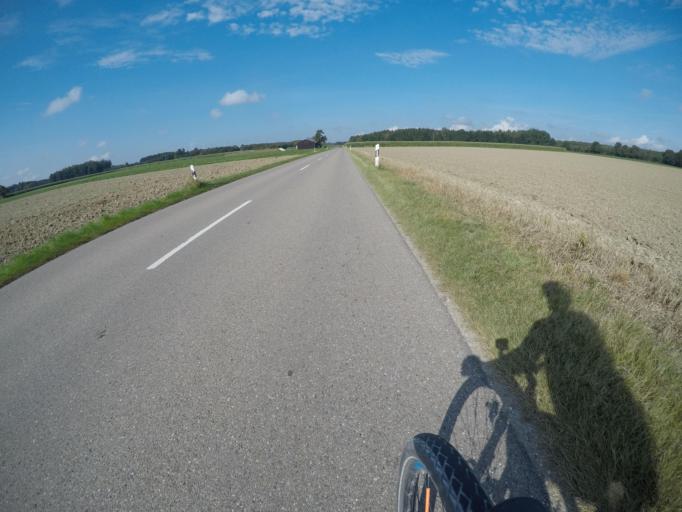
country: DE
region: Bavaria
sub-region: Swabia
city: Allmannshofen
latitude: 48.6141
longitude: 10.7997
